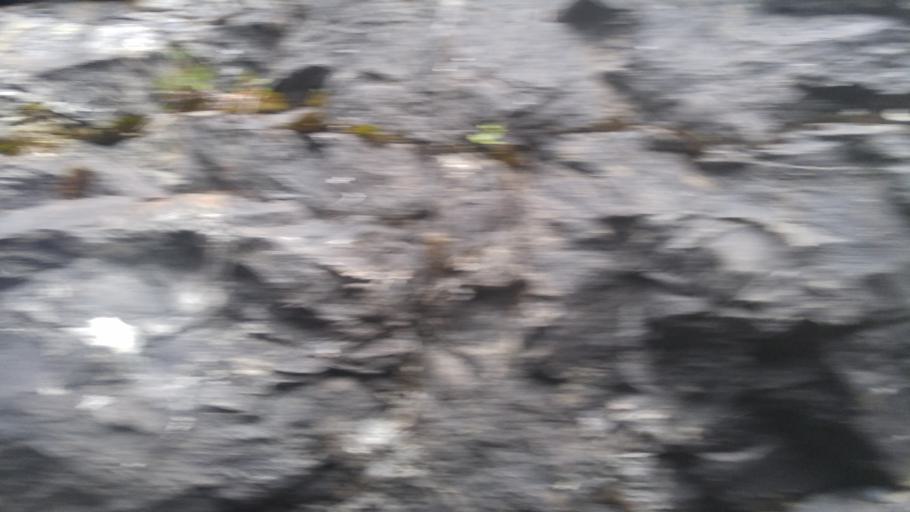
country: NO
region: Nord-Trondelag
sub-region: Stjordal
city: Stjordal
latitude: 63.4457
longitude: 10.9199
